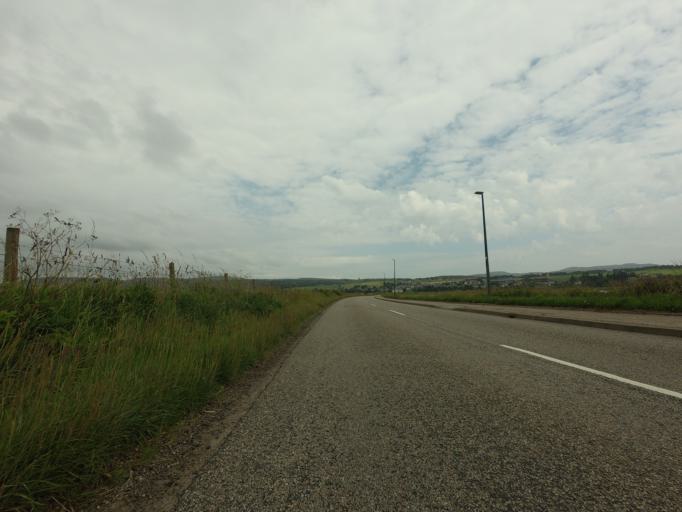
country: GB
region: Scotland
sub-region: Highland
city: Alness
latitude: 57.8861
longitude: -4.3593
